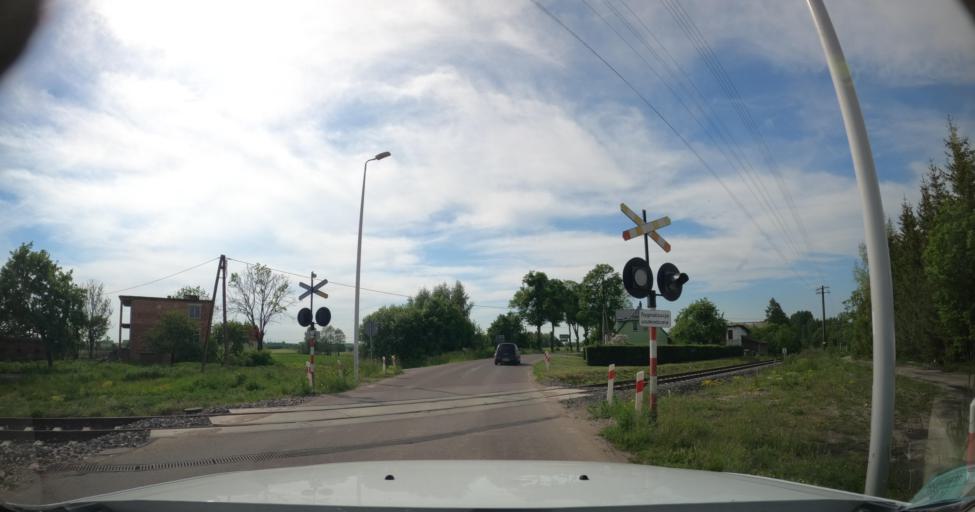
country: PL
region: Warmian-Masurian Voivodeship
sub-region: Powiat lidzbarski
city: Lubomino
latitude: 54.0671
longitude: 20.2325
